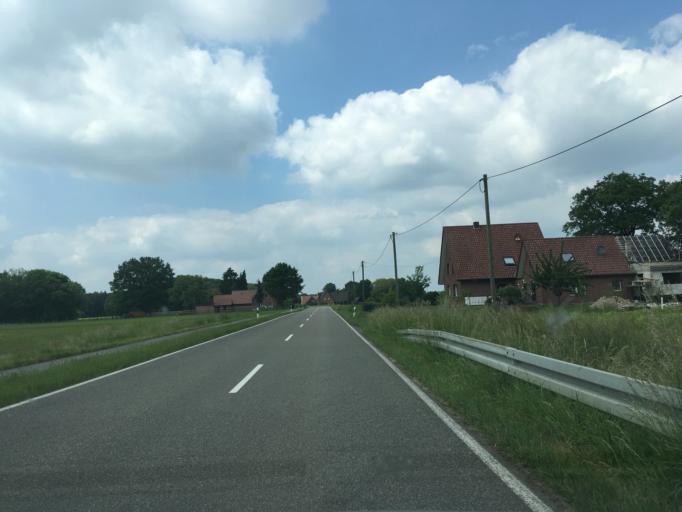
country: DE
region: North Rhine-Westphalia
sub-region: Regierungsbezirk Munster
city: Rhede
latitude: 51.7893
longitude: 6.7664
